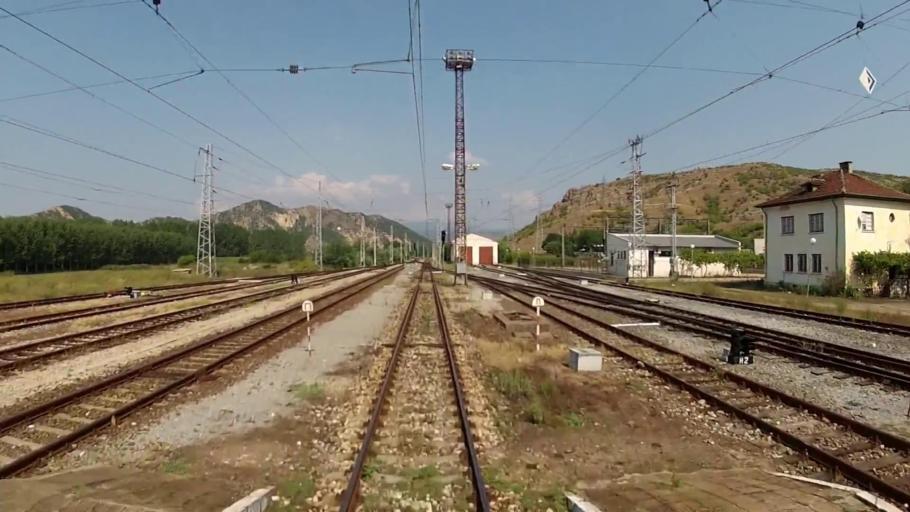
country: BG
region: Blagoevgrad
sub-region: Obshtina Petrich
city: Petrich
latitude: 41.4597
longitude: 23.2721
